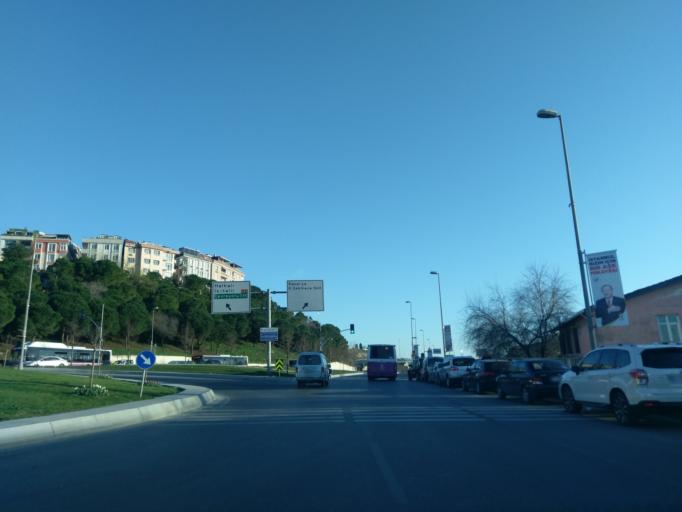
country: TR
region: Istanbul
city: Mahmutbey
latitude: 41.0199
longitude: 28.7679
